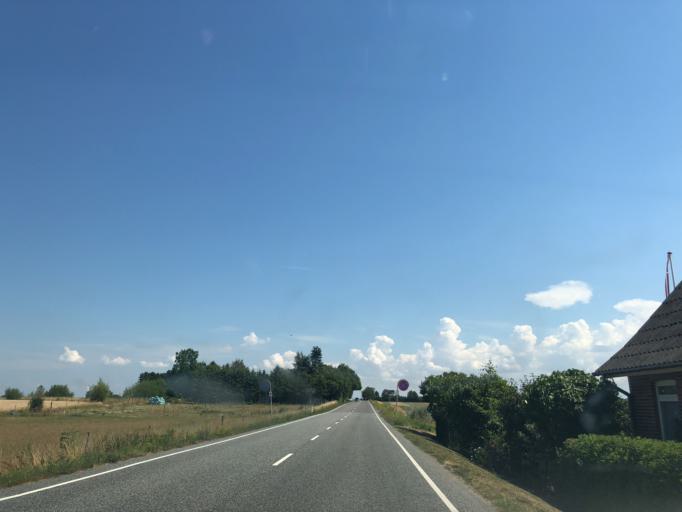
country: DK
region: Zealand
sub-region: Naestved Kommune
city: Fuglebjerg
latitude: 55.2922
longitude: 11.4291
